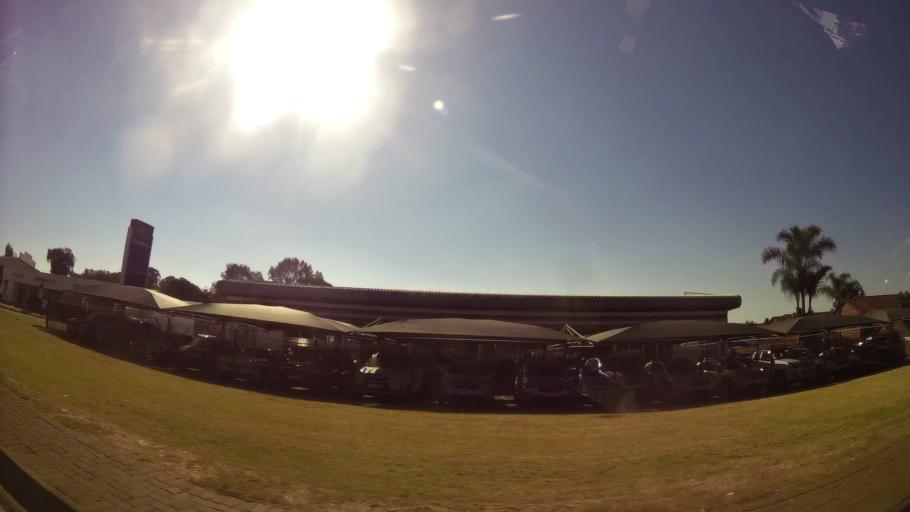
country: ZA
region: Gauteng
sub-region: City of Tshwane Metropolitan Municipality
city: Centurion
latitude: -25.8622
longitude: 28.1648
